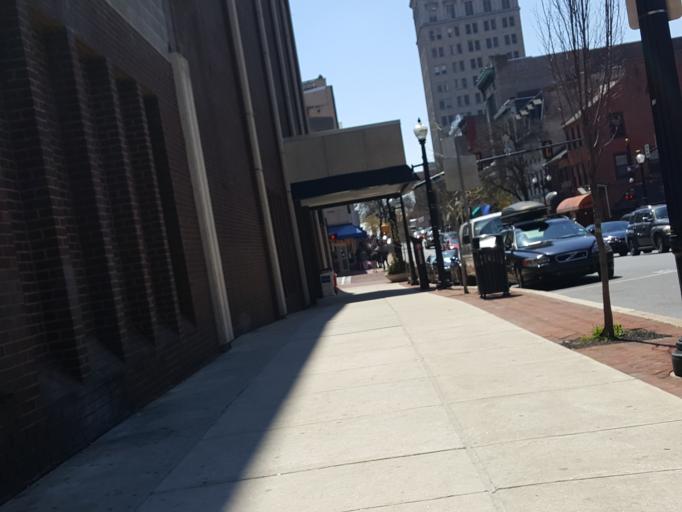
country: US
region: Pennsylvania
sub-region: Lancaster County
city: Lancaster
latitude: 40.0401
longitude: -76.3061
